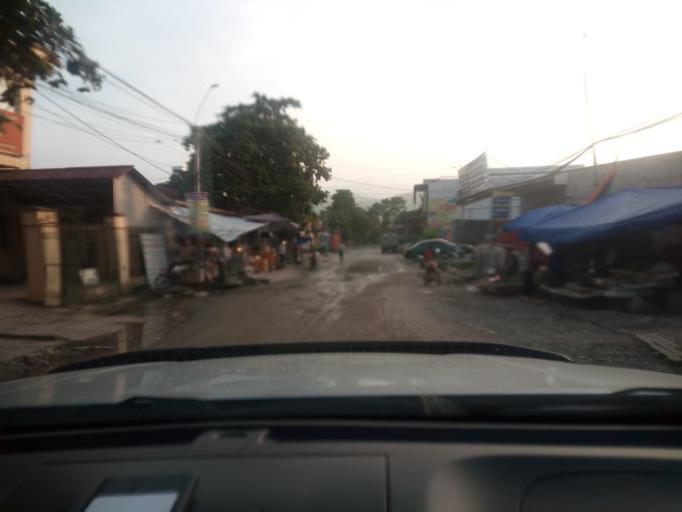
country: VN
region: Yen Bai
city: Co Phuc
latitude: 21.8676
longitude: 104.6502
